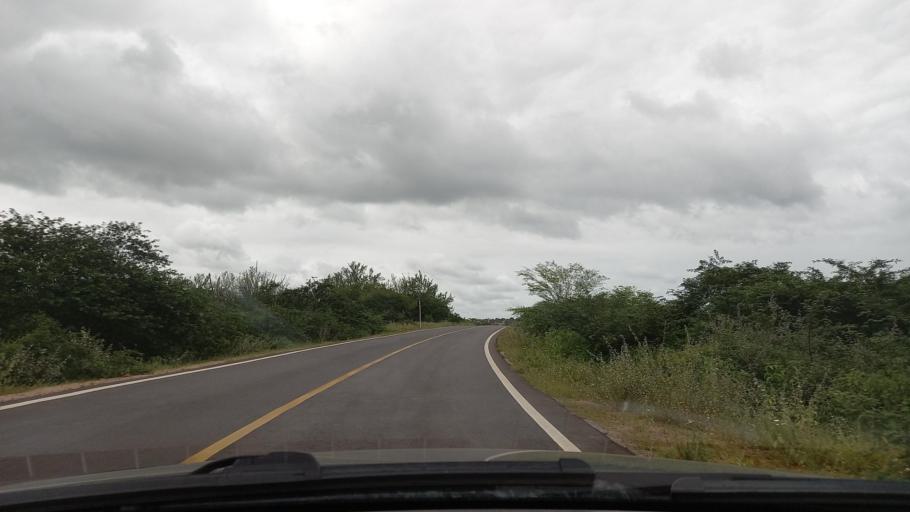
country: BR
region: Sergipe
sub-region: Caninde De Sao Francisco
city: Caninde de Sao Francisco
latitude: -9.6179
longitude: -37.7800
